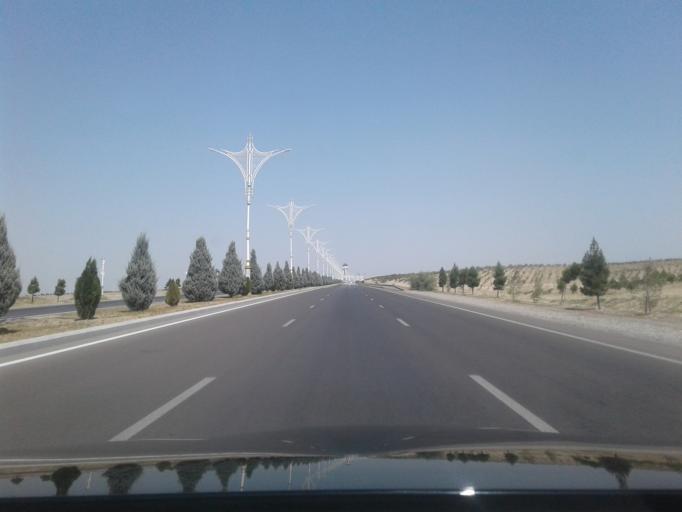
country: TM
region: Ahal
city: Ashgabat
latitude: 37.8783
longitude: 58.4095
